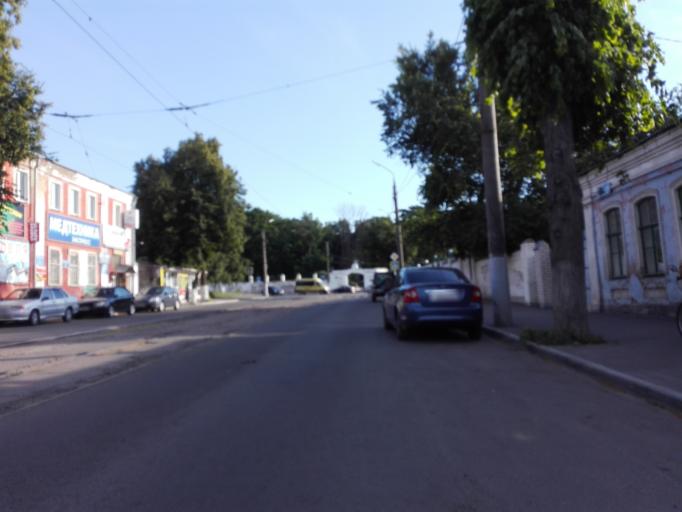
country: RU
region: Orjol
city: Orel
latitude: 52.9514
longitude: 36.0532
